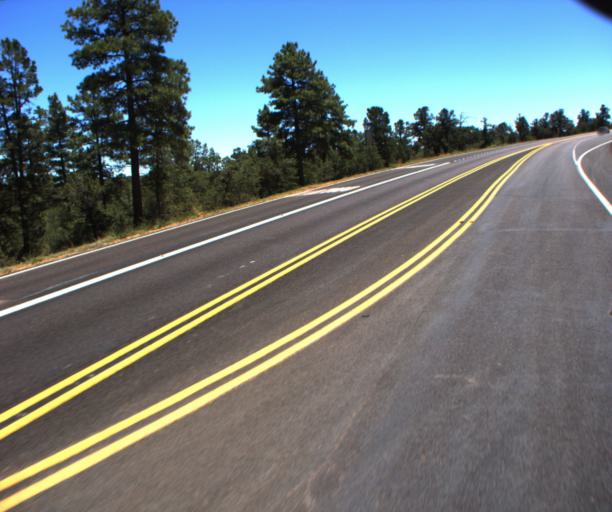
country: US
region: Arizona
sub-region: Gila County
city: Pine
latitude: 34.3600
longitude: -111.4248
